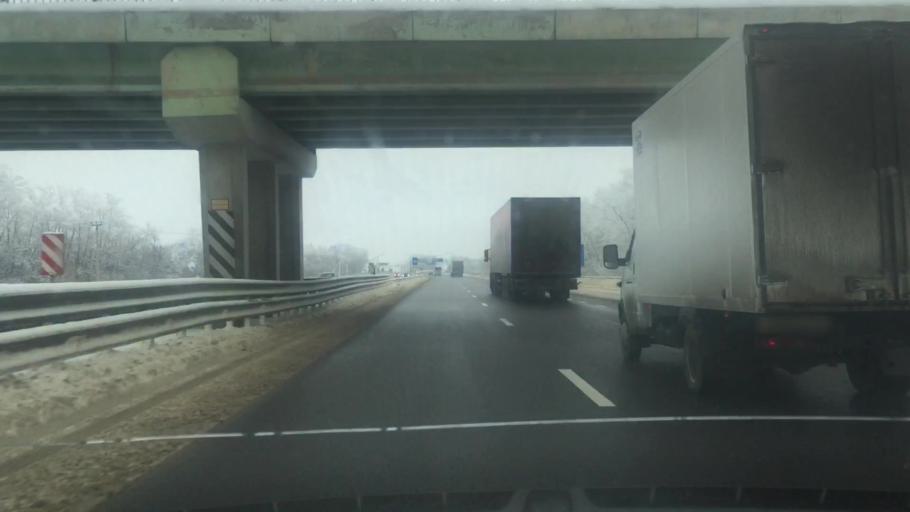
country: RU
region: Tula
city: Kazachka
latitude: 53.2992
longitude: 38.1781
